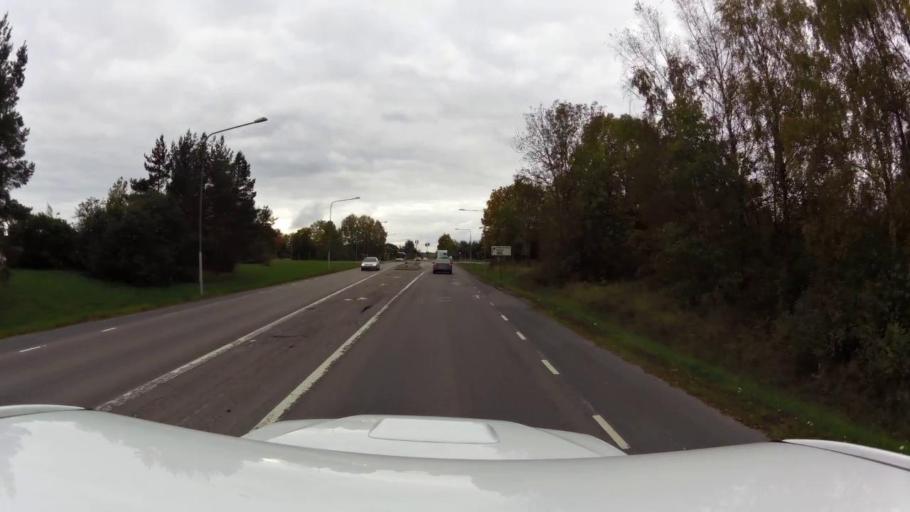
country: SE
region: OEstergoetland
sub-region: Linkopings Kommun
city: Ljungsbro
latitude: 58.4947
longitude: 15.5017
